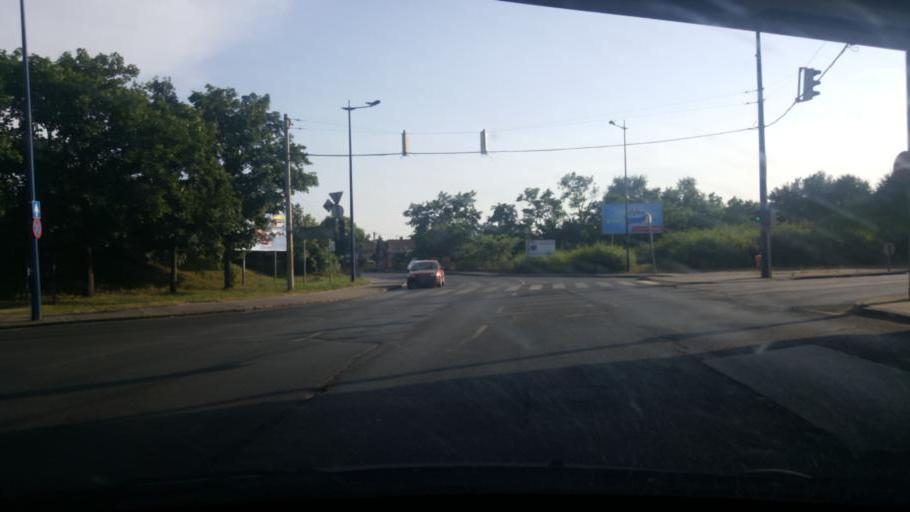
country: HU
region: Budapest
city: Budapest XVIII. keruelet
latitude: 47.4532
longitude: 19.1960
